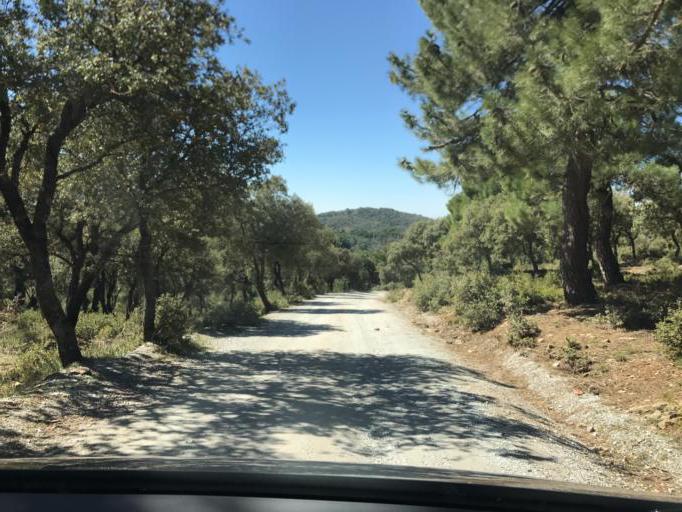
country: ES
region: Andalusia
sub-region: Provincia de Granada
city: Viznar
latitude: 37.2615
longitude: -3.5279
